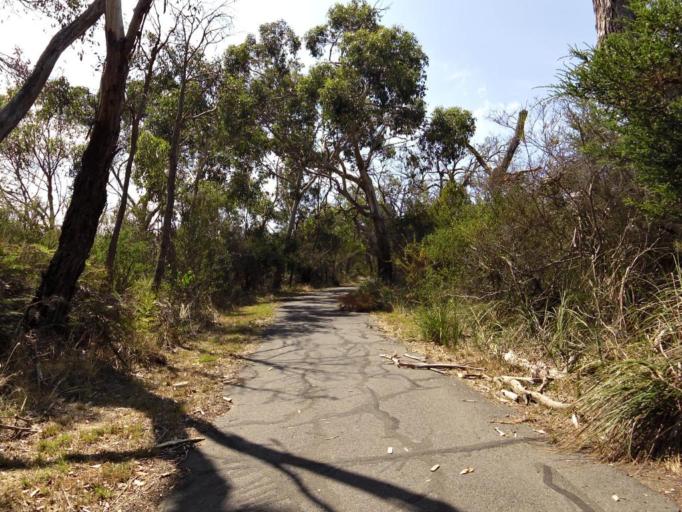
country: AU
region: Victoria
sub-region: Mornington Peninsula
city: Crib Point
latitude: -38.3511
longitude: 145.1673
